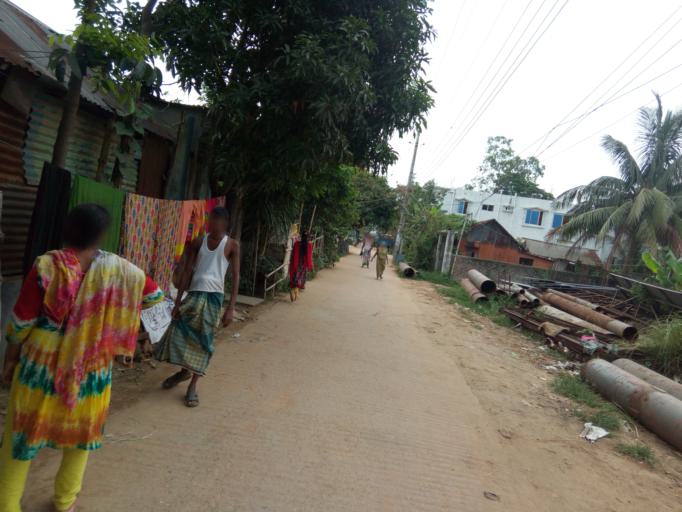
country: BD
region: Dhaka
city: Paltan
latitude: 23.7380
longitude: 90.4552
